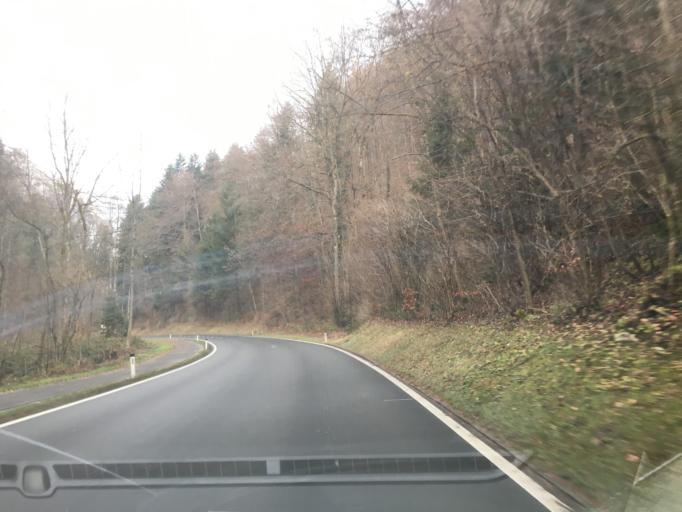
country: AT
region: Vorarlberg
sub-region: Politischer Bezirk Feldkirch
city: Klaus
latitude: 47.3174
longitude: 9.6451
